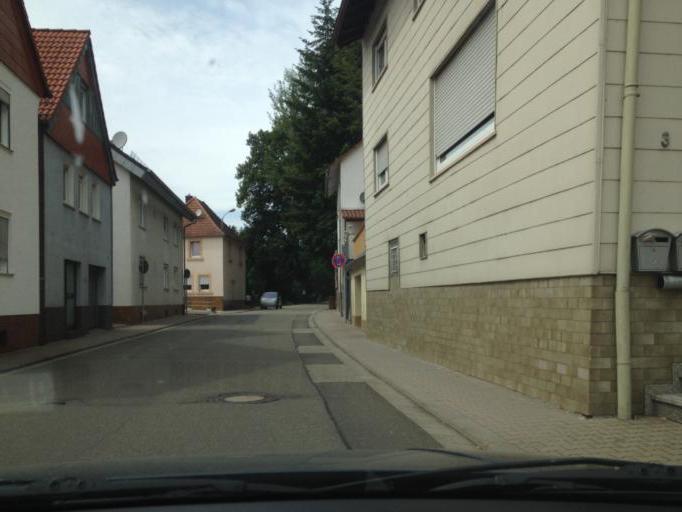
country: DE
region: Rheinland-Pfalz
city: Linden
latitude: 49.3519
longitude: 7.6433
